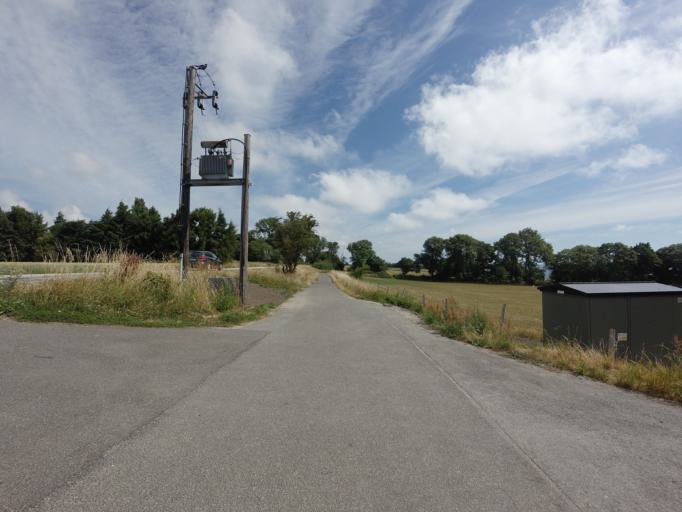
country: SE
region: Skane
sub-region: Simrishamns Kommun
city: Simrishamn
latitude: 55.5038
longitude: 14.3281
